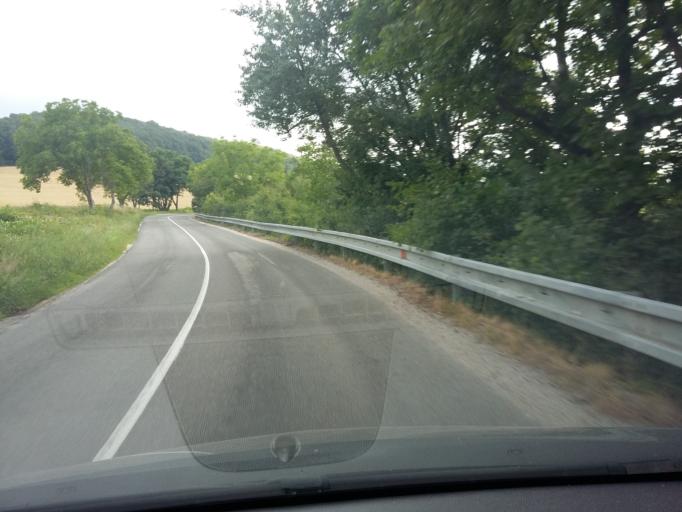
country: SK
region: Trnavsky
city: Smolenice
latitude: 48.5376
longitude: 17.3602
